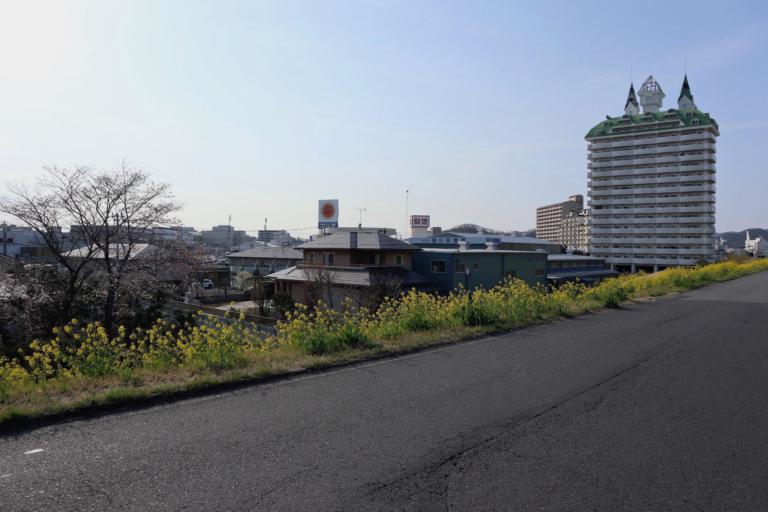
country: JP
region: Tochigi
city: Ashikaga
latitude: 36.3201
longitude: 139.4553
